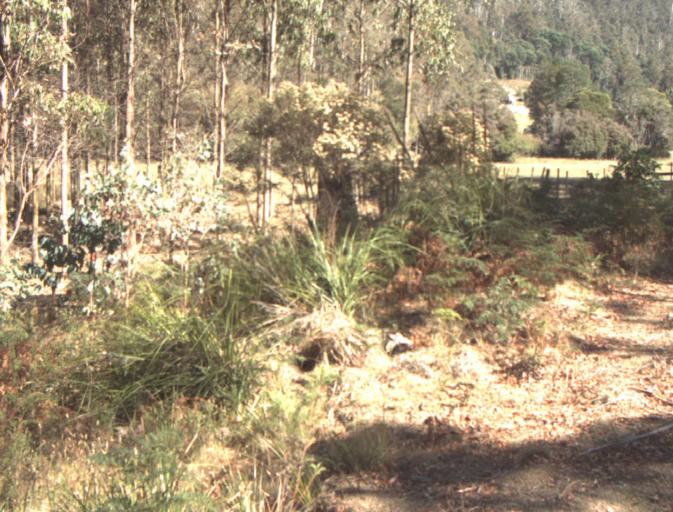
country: AU
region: Tasmania
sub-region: Launceston
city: Newstead
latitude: -41.3027
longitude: 147.3152
